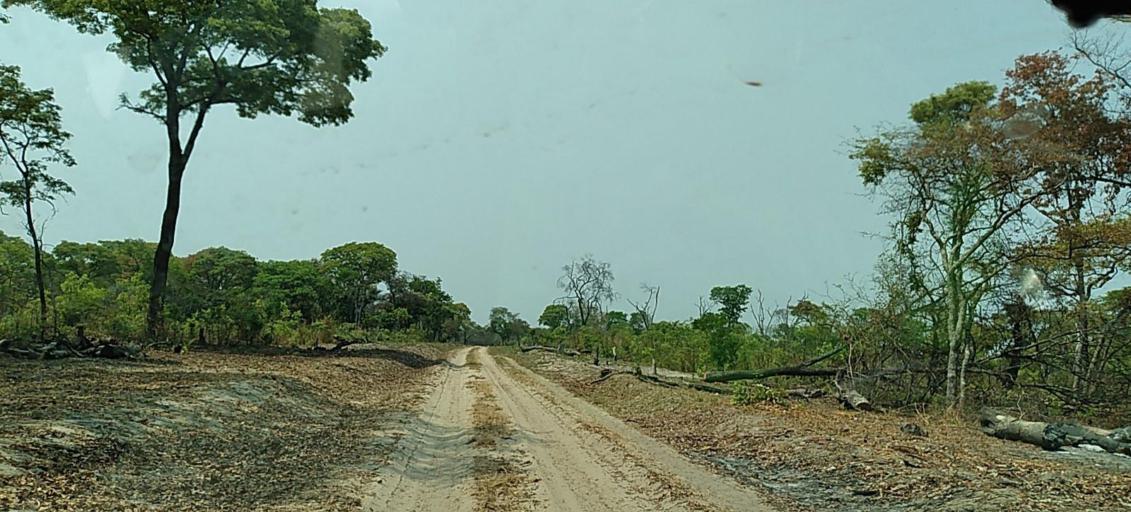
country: ZM
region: Western
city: Lukulu
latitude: -13.9604
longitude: 23.2249
